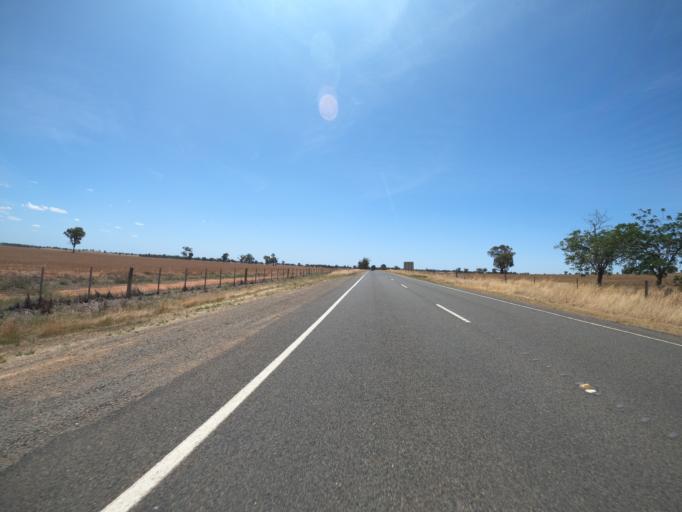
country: AU
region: Victoria
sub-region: Moira
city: Yarrawonga
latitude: -36.1551
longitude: 145.9672
